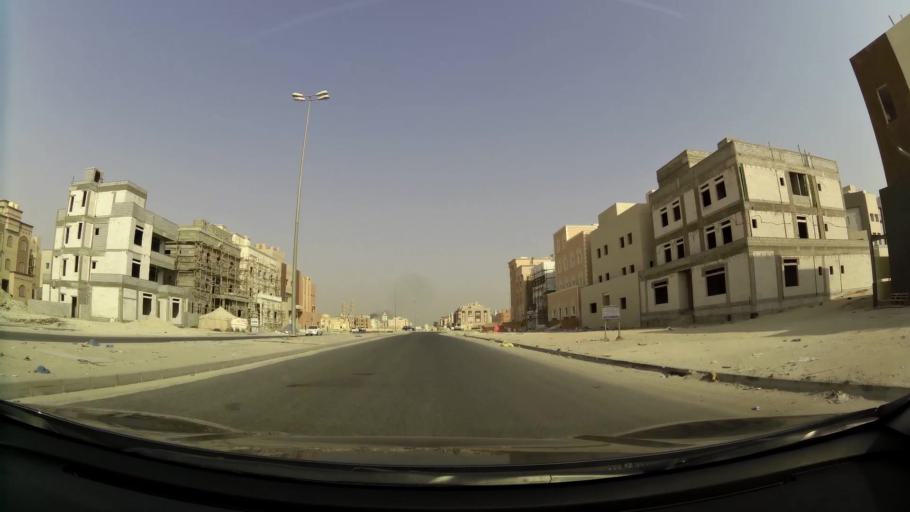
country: KW
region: Muhafazat al Jahra'
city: Al Jahra'
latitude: 29.3454
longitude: 47.7470
